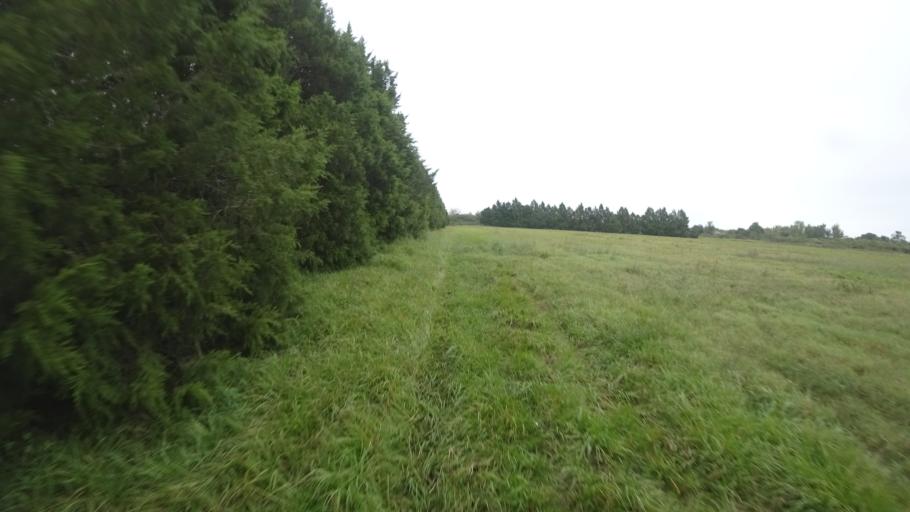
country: US
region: Florida
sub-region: Sarasota County
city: Warm Mineral Springs
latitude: 27.3011
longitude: -82.1296
